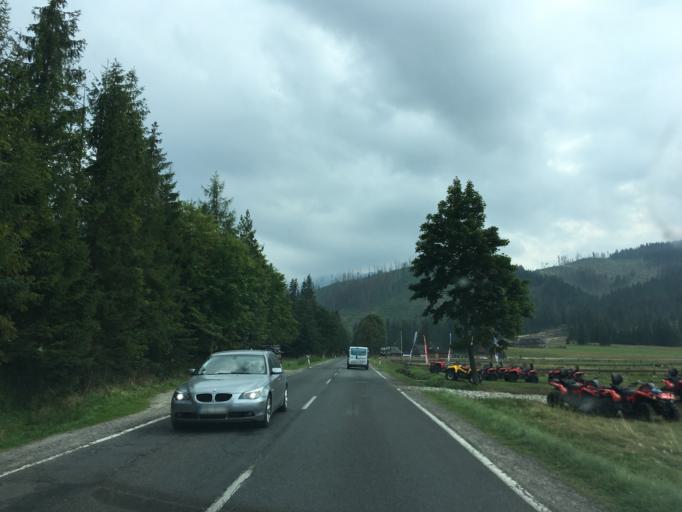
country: PL
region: Lesser Poland Voivodeship
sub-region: Powiat tatrzanski
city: Koscielisko
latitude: 49.2841
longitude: 19.8553
